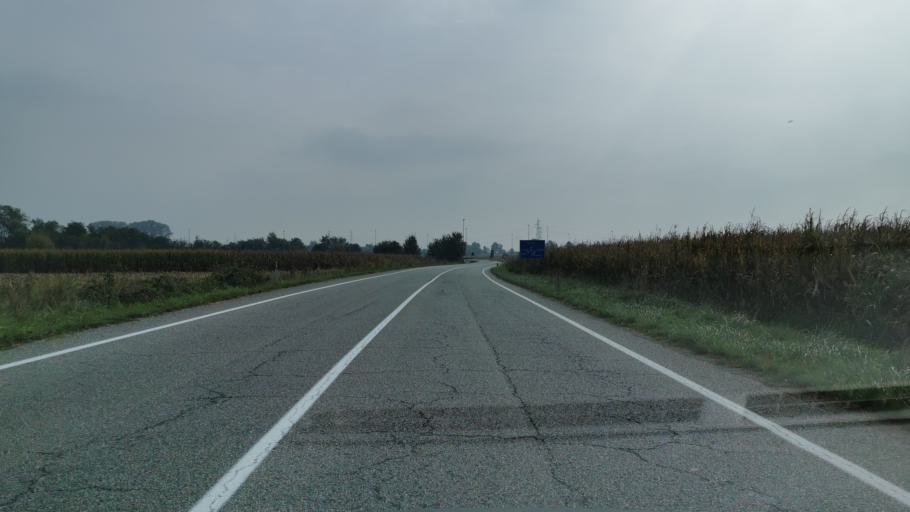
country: IT
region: Piedmont
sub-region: Provincia di Torino
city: Montanaro
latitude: 45.2294
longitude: 7.8877
